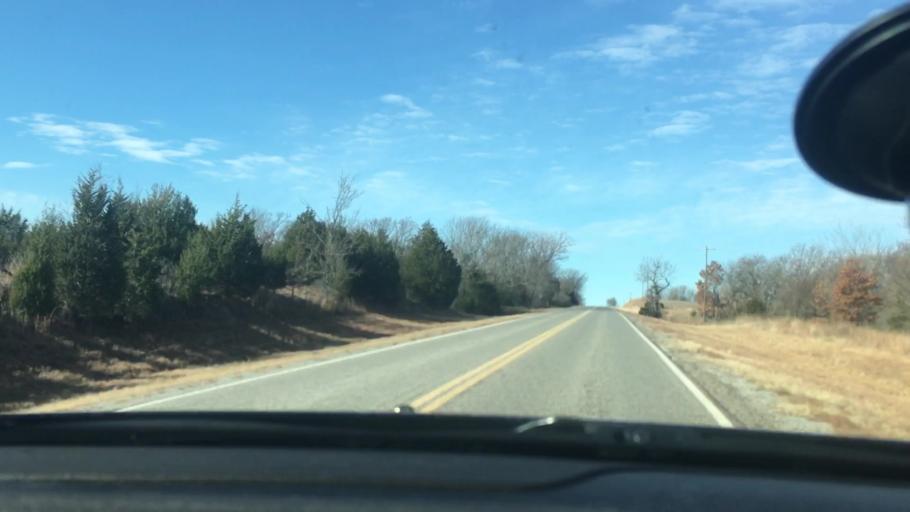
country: US
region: Oklahoma
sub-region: Seminole County
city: Konawa
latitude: 34.9854
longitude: -96.8958
